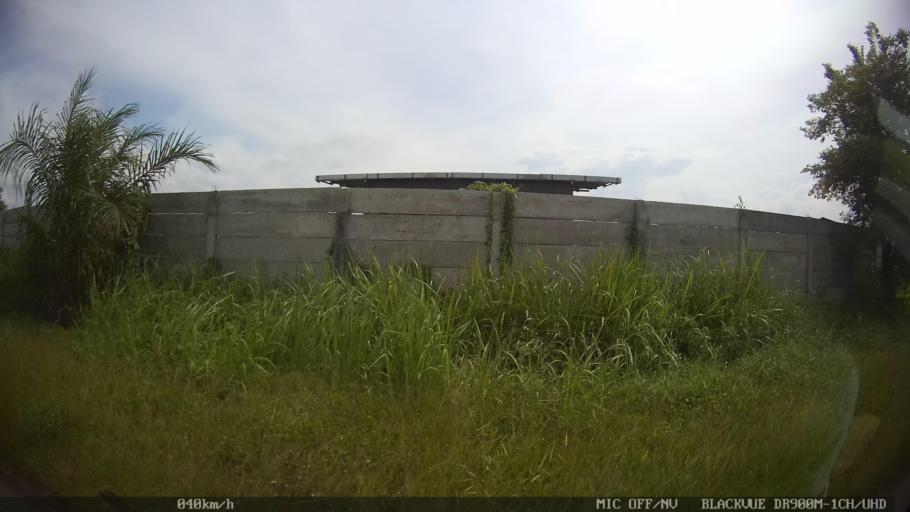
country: ID
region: North Sumatra
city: Percut
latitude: 3.6150
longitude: 98.8411
